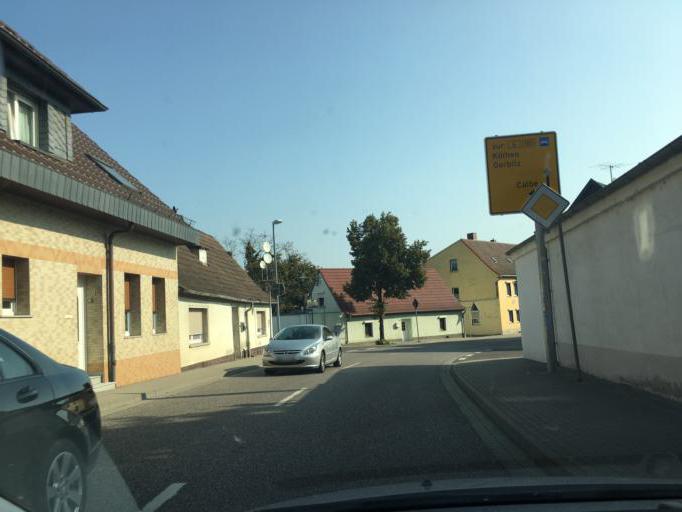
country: DE
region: Saxony-Anhalt
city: Nienburg/Saale
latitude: 51.8399
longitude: 11.7679
